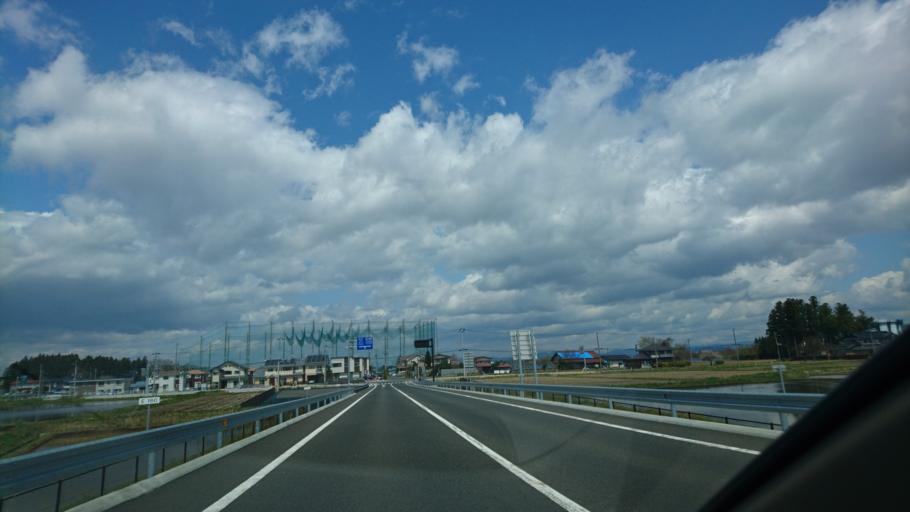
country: JP
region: Iwate
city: Mizusawa
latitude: 39.1166
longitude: 141.1249
